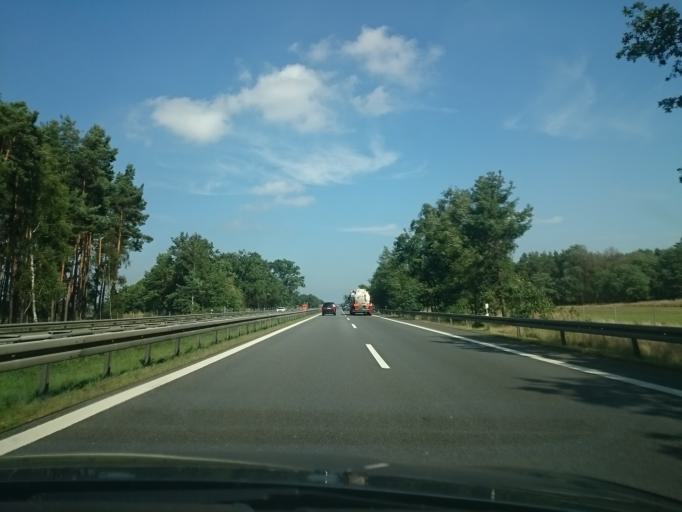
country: DE
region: Brandenburg
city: Calau
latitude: 51.7510
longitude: 13.8622
